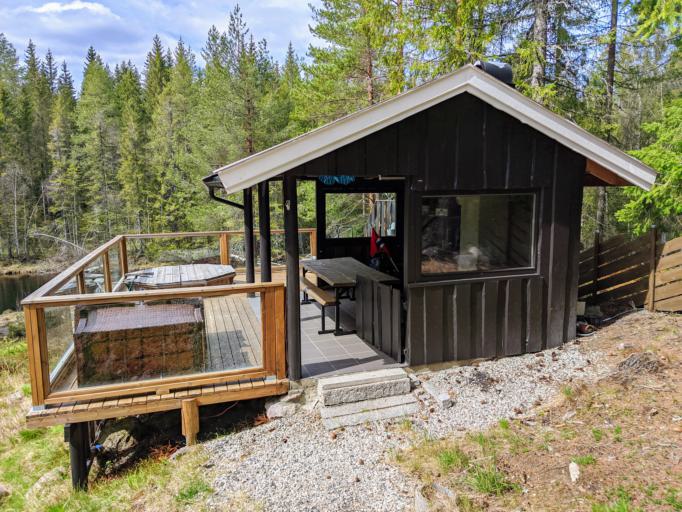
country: NO
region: Akershus
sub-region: Nittedal
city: Aneby
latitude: 60.1934
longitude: 10.9064
